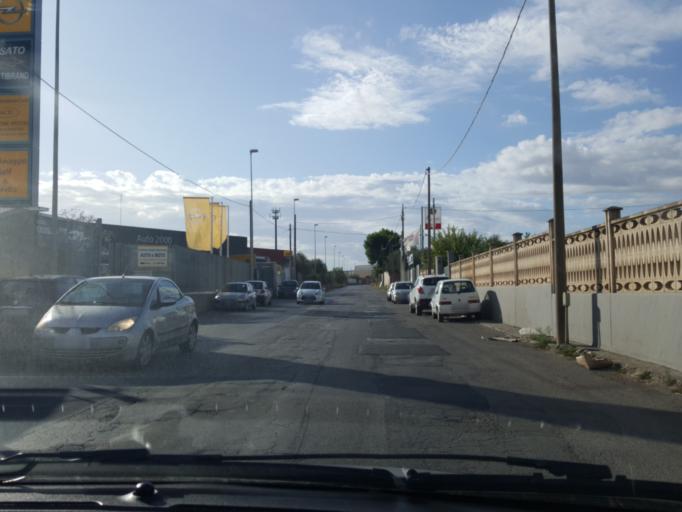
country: IT
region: Apulia
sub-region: Provincia di Bari
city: Triggiano
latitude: 41.0643
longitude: 16.9341
